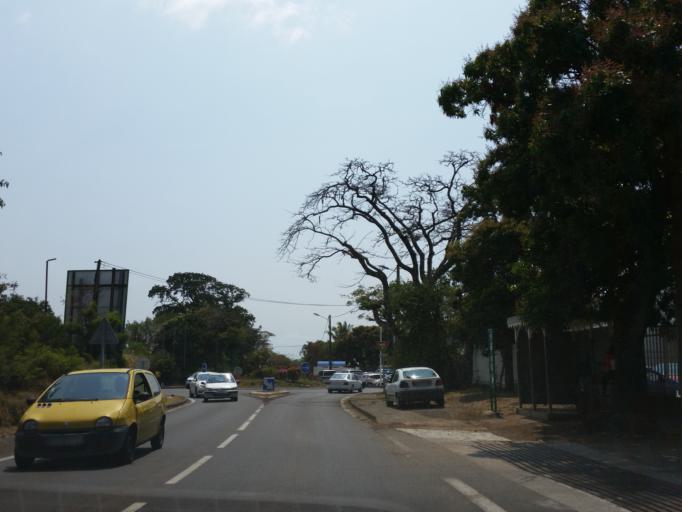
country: RE
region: Reunion
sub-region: Reunion
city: Sainte-Marie
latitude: -20.9028
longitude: 55.5075
